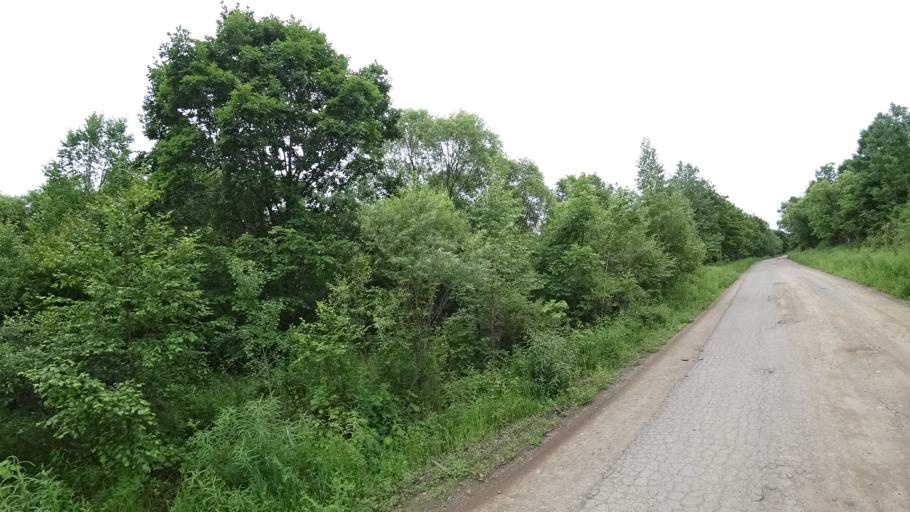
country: RU
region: Primorskiy
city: Novosysoyevka
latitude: 44.2025
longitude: 133.3213
